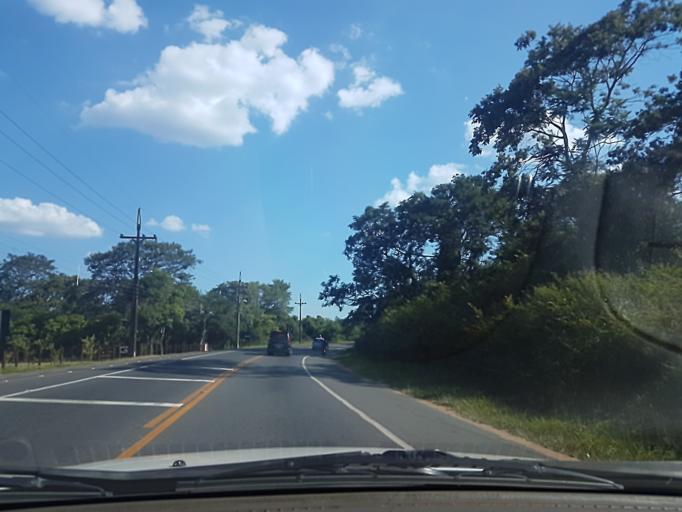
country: PY
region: Central
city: Aregua
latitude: -25.2290
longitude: -57.4180
